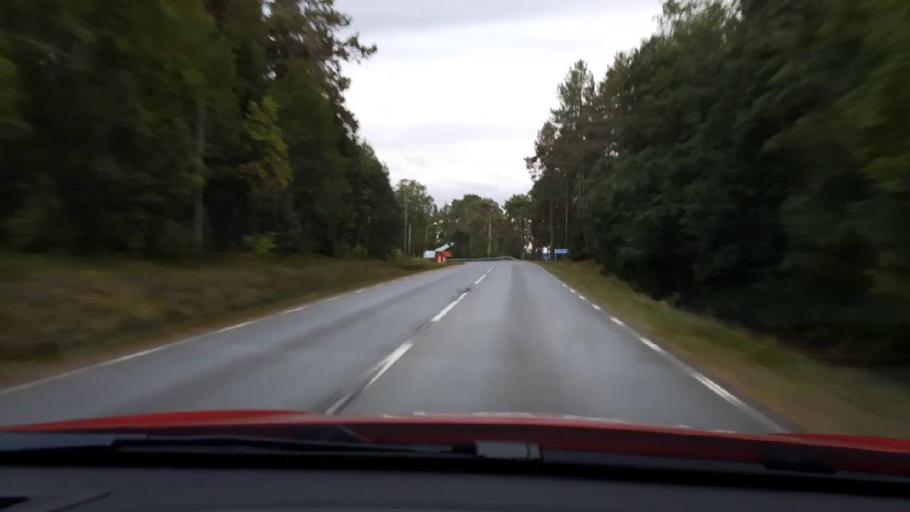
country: SE
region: Jaemtland
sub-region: Bergs Kommun
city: Hoverberg
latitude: 62.9894
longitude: 14.4824
